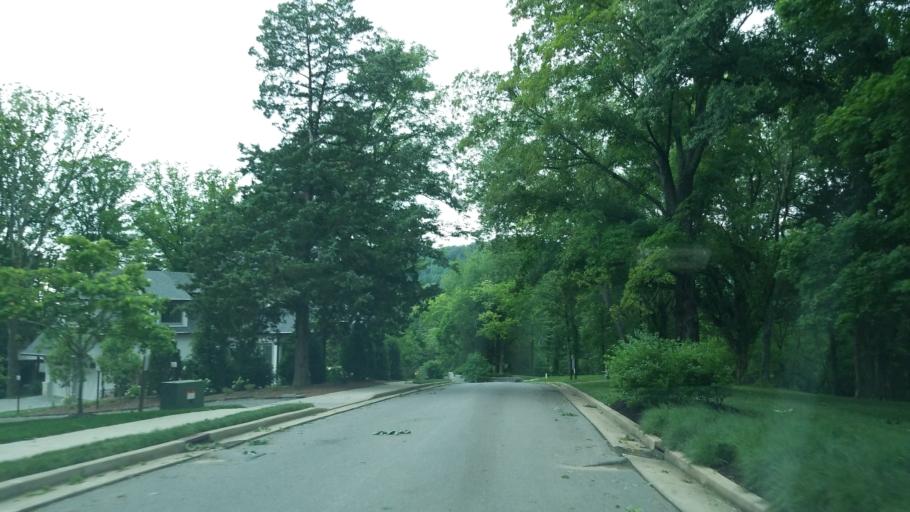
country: US
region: Tennessee
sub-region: Davidson County
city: Forest Hills
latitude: 36.0496
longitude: -86.8143
